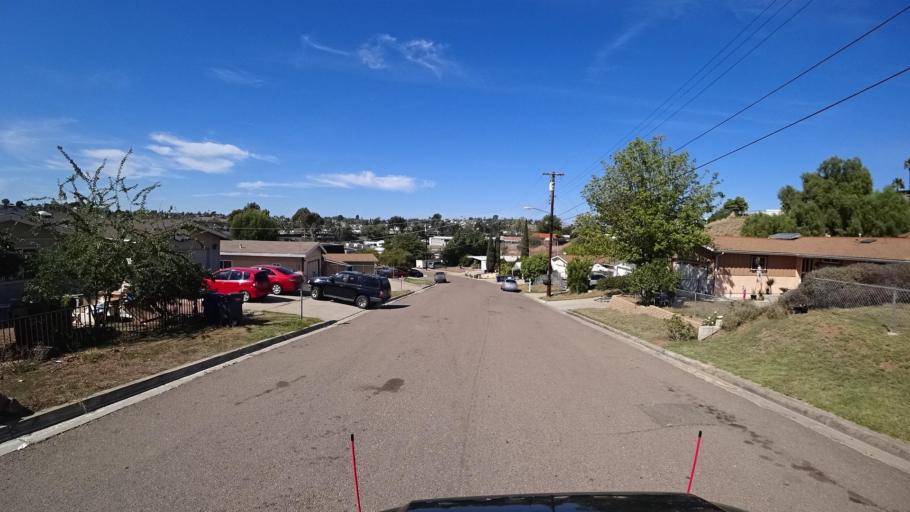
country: US
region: California
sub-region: San Diego County
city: La Presa
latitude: 32.7210
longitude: -117.0118
